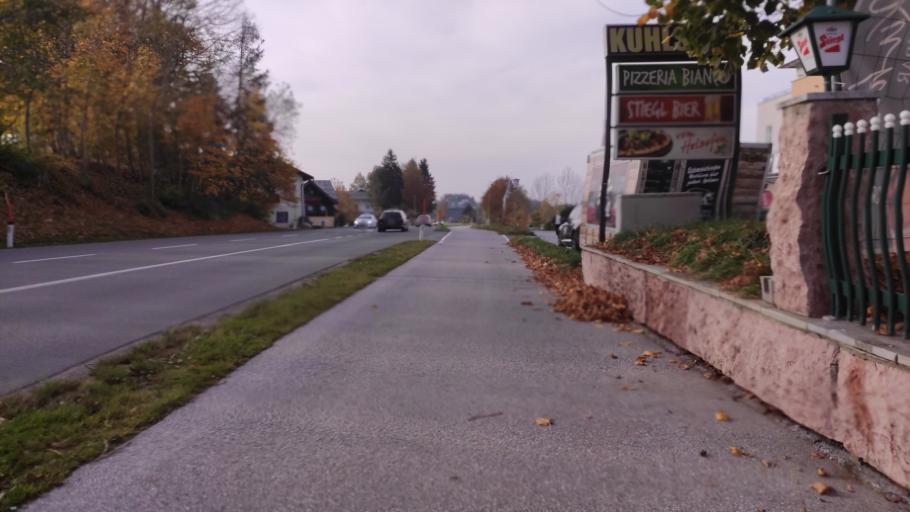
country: AT
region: Salzburg
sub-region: Politischer Bezirk Salzburg-Umgebung
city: Hof bei Salzburg
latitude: 47.8170
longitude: 13.2273
